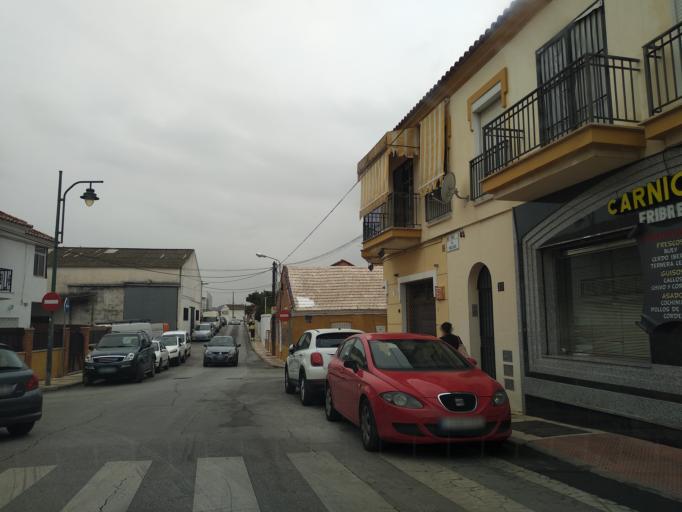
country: ES
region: Andalusia
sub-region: Provincia de Malaga
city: Malaga
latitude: 36.7401
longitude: -4.4799
